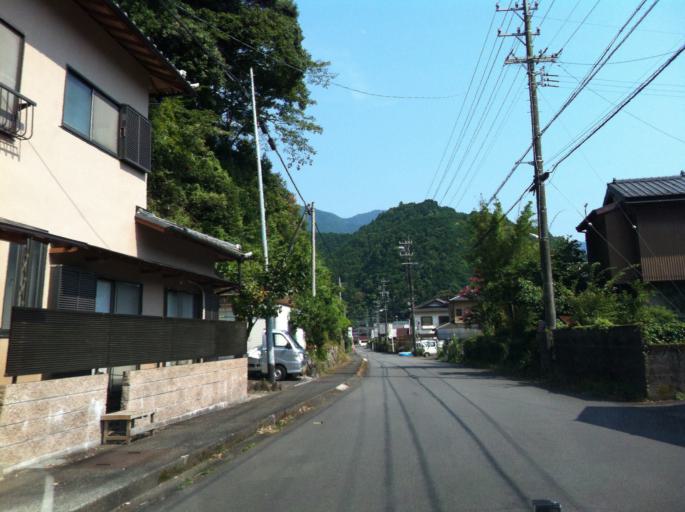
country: JP
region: Shizuoka
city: Shizuoka-shi
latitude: 35.1100
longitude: 138.3633
